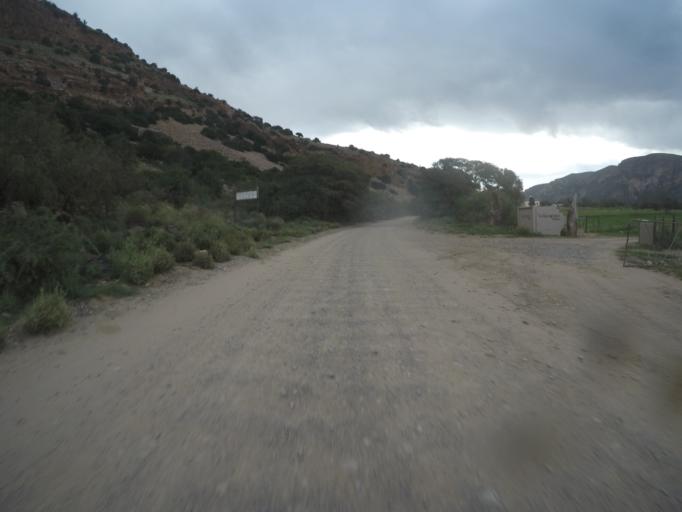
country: ZA
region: Eastern Cape
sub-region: Cacadu District Municipality
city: Willowmore
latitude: -33.5251
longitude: 23.8452
